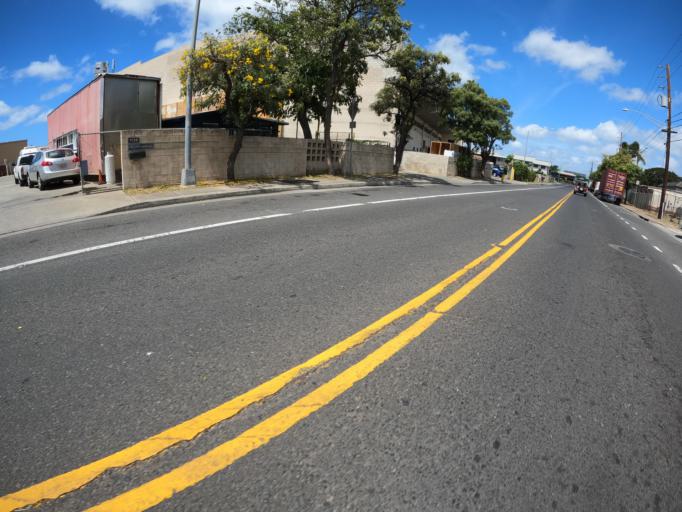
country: US
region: Hawaii
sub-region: Honolulu County
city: Honolulu
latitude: 21.3057
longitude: -157.8741
